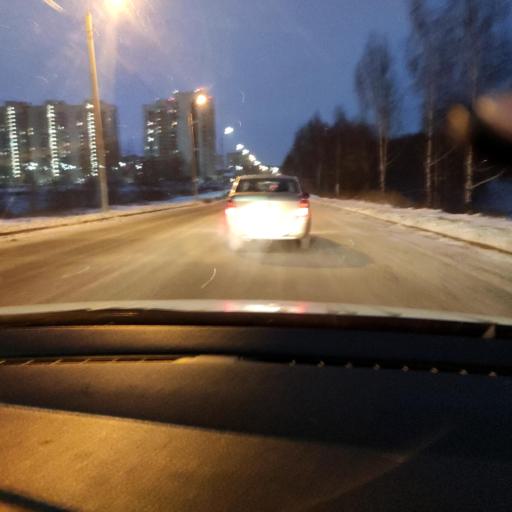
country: RU
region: Tatarstan
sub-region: Zelenodol'skiy Rayon
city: Zelenodolsk
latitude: 55.8685
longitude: 48.5682
